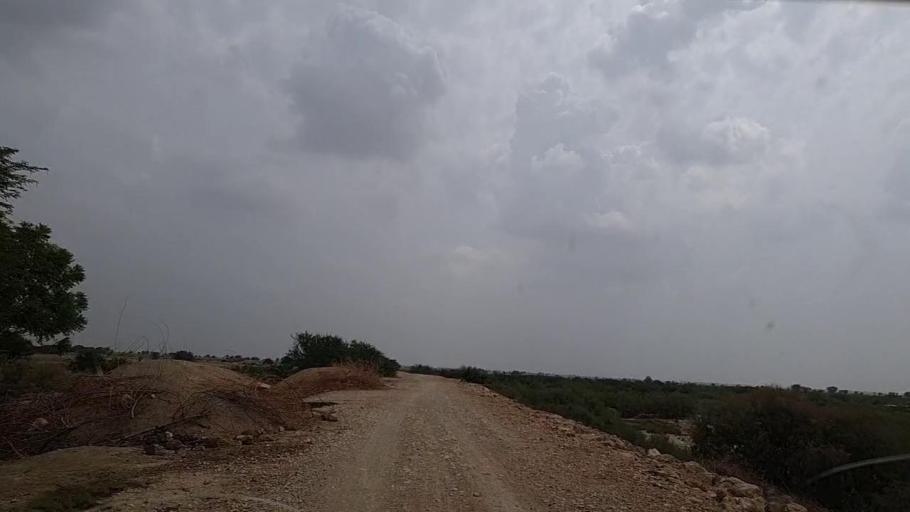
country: PK
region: Sindh
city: Johi
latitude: 26.7318
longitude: 67.5792
